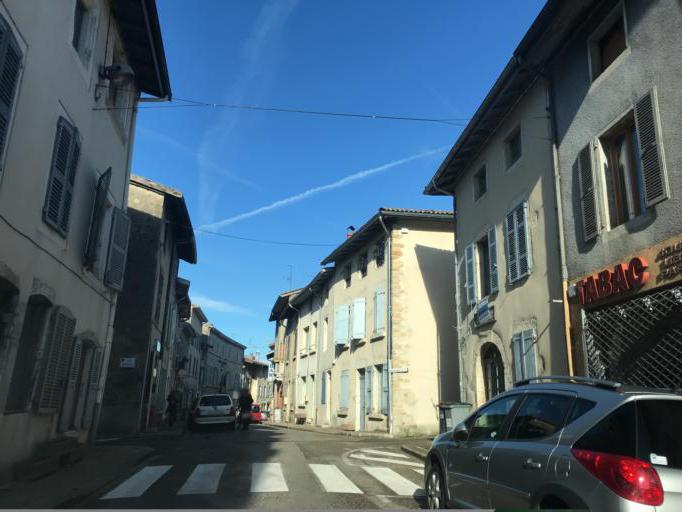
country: FR
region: Rhone-Alpes
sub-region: Departement de l'Ain
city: Ambronay
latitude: 46.0062
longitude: 5.3603
